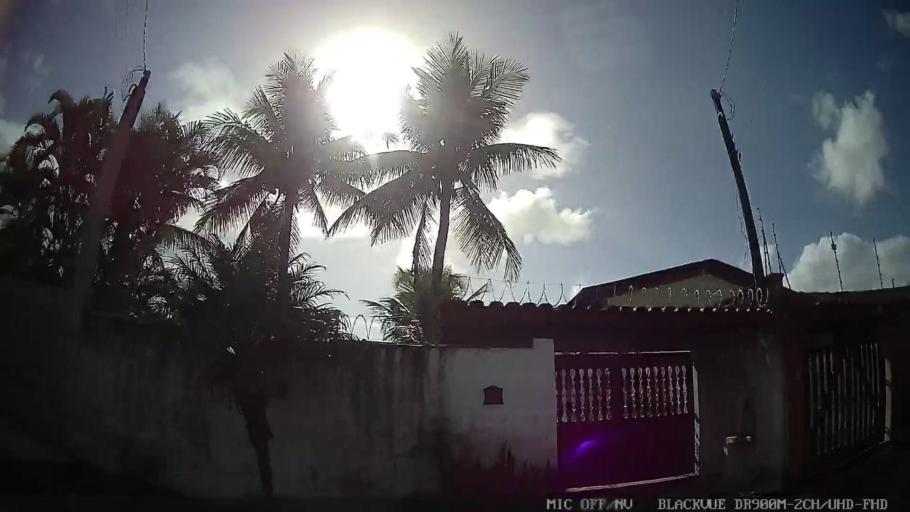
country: BR
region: Sao Paulo
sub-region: Itanhaem
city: Itanhaem
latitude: -24.2055
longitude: -46.8323
